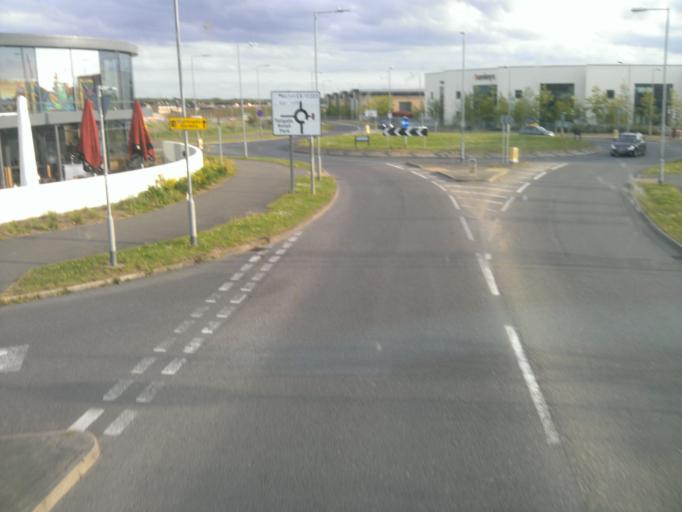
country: GB
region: England
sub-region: Essex
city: Eight Ash Green
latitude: 51.8852
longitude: 0.8273
